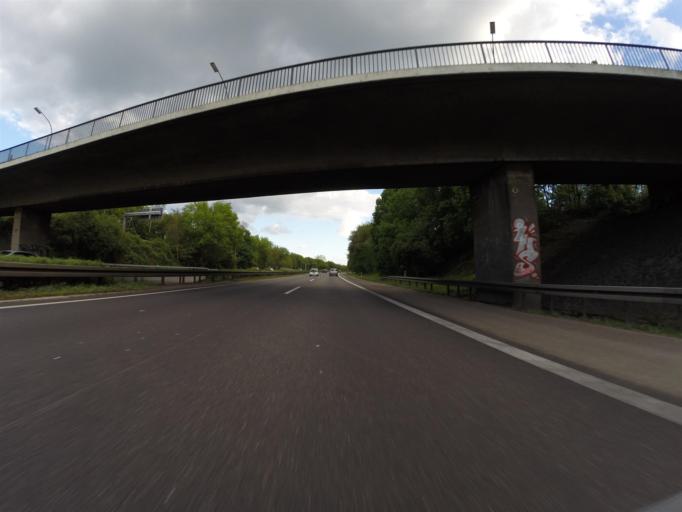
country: DE
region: Saarland
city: Saarbrucken
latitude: 49.2198
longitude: 7.0167
